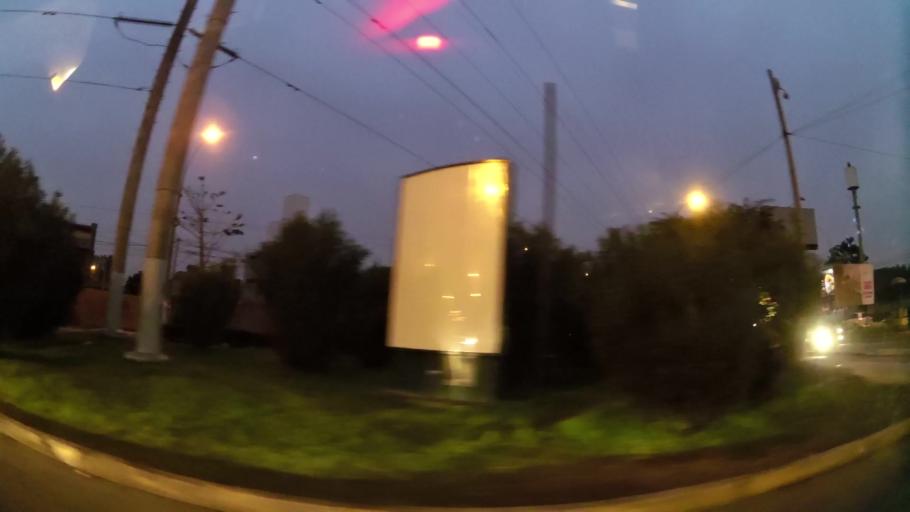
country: PE
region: Lima
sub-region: Lima
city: La Molina
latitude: -12.0771
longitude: -76.9542
